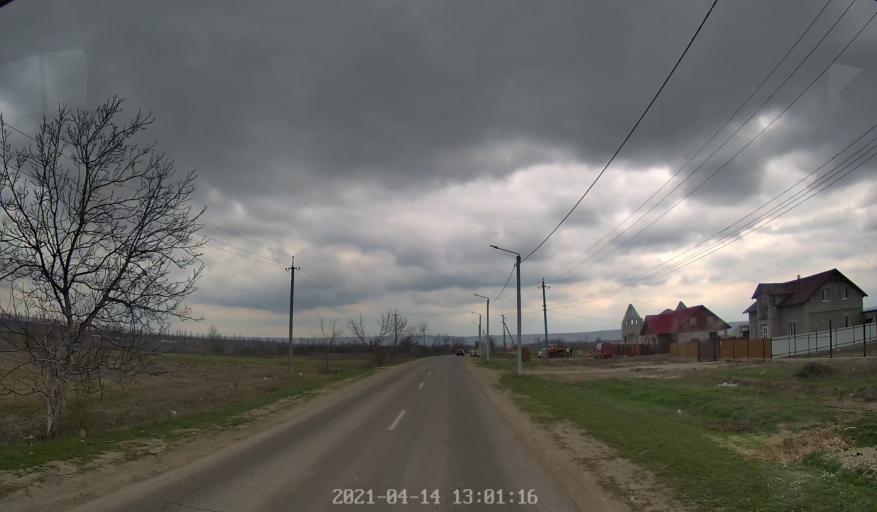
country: MD
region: Chisinau
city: Vadul lui Voda
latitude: 47.1330
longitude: 29.1173
